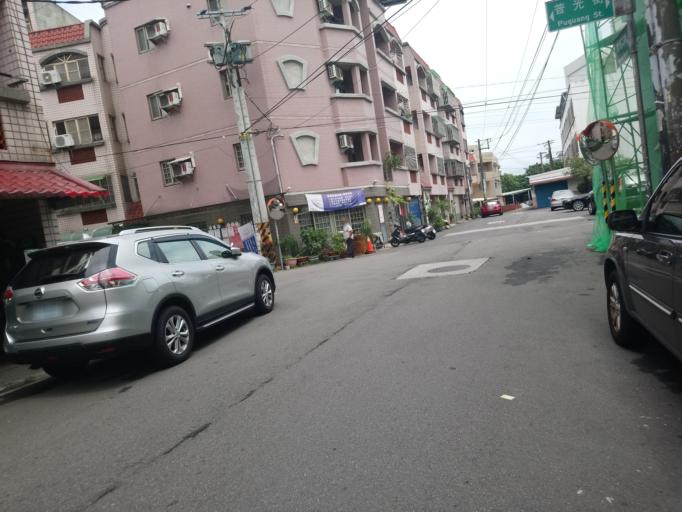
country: TW
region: Taiwan
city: Taoyuan City
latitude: 24.9497
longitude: 121.2463
